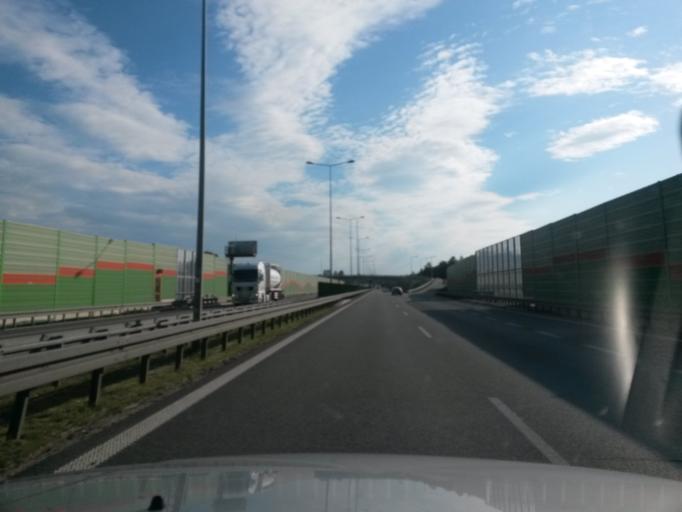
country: PL
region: Lodz Voivodeship
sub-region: Powiat rawski
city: Rawa Mazowiecka
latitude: 51.7510
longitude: 20.2482
